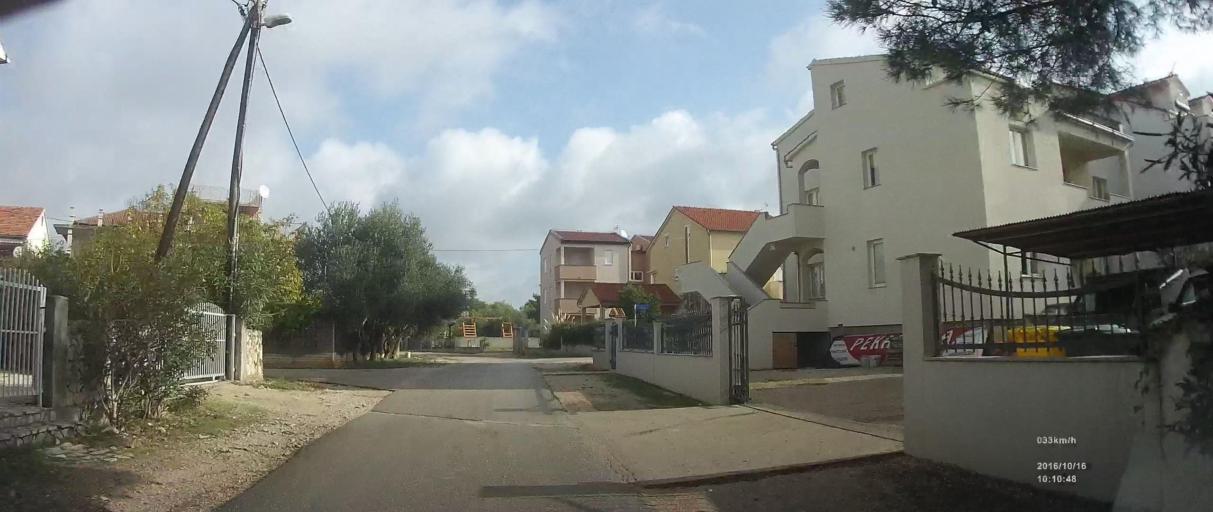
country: HR
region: Zadarska
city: Pakostane
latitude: 43.9136
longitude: 15.5067
